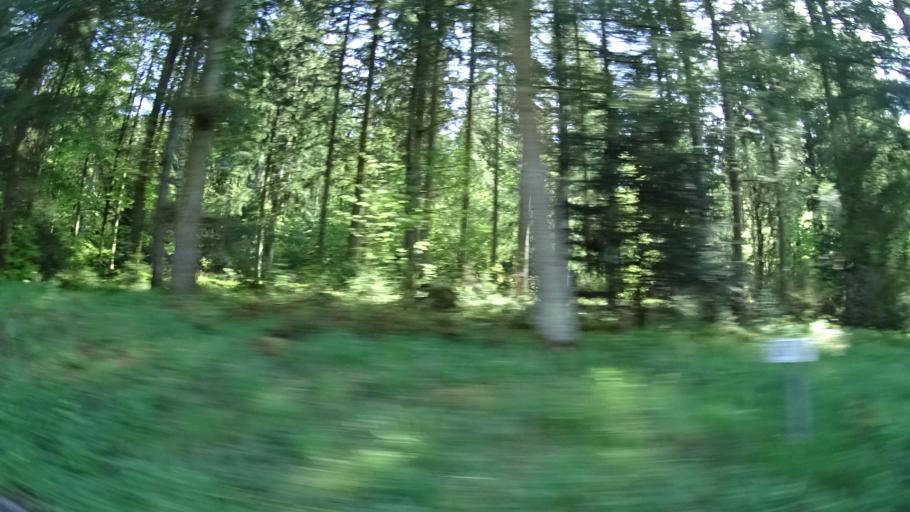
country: DE
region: Baden-Wuerttemberg
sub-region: Karlsruhe Region
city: Bad Wildbad
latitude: 48.7139
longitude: 8.5621
